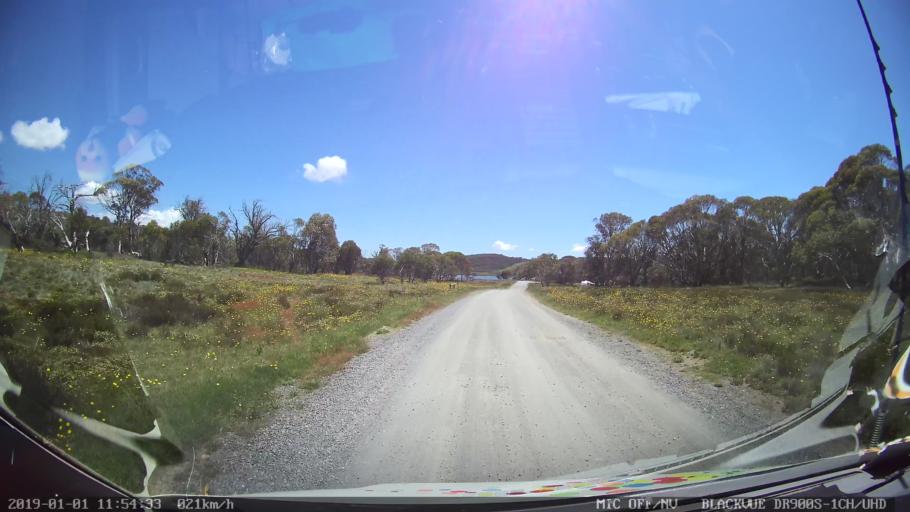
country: AU
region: New South Wales
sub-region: Snowy River
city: Jindabyne
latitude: -35.8909
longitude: 148.4480
